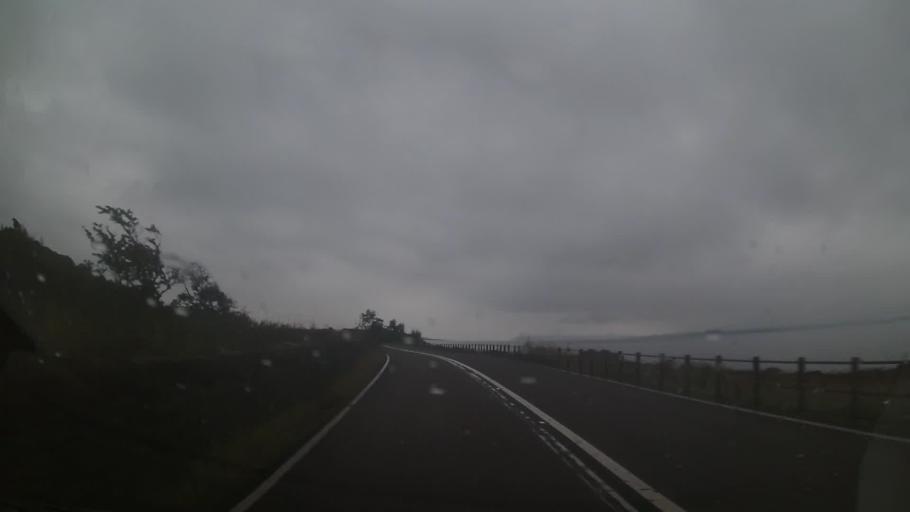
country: GB
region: Scotland
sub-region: North Ayrshire
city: Skelmorlie
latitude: 55.8288
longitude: -4.8886
